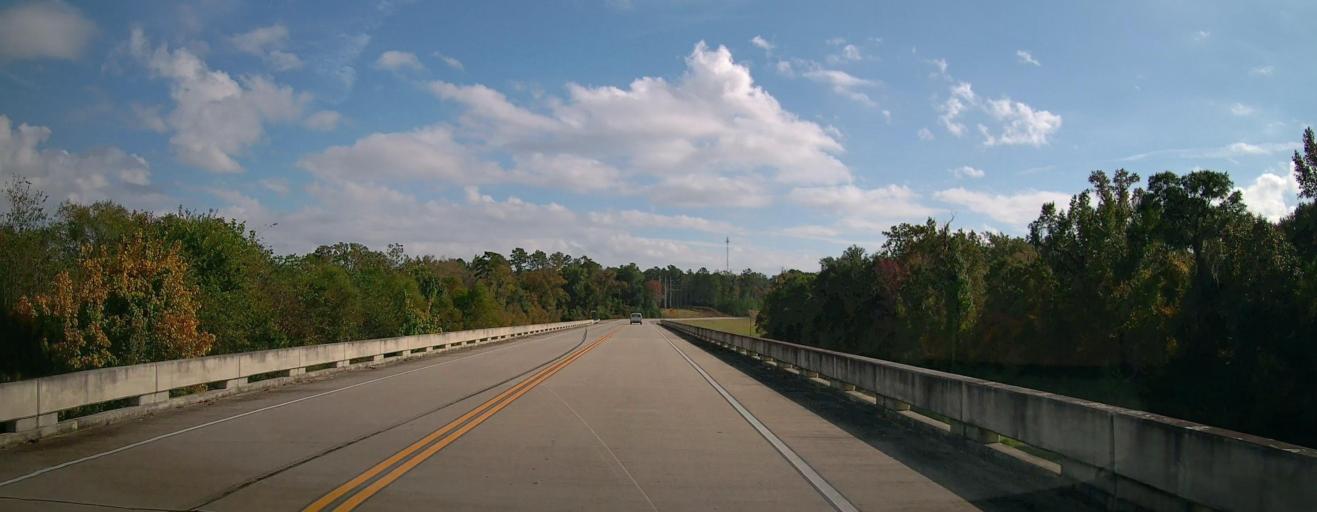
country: US
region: Georgia
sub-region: Thomas County
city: Thomasville
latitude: 30.9123
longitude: -84.0082
